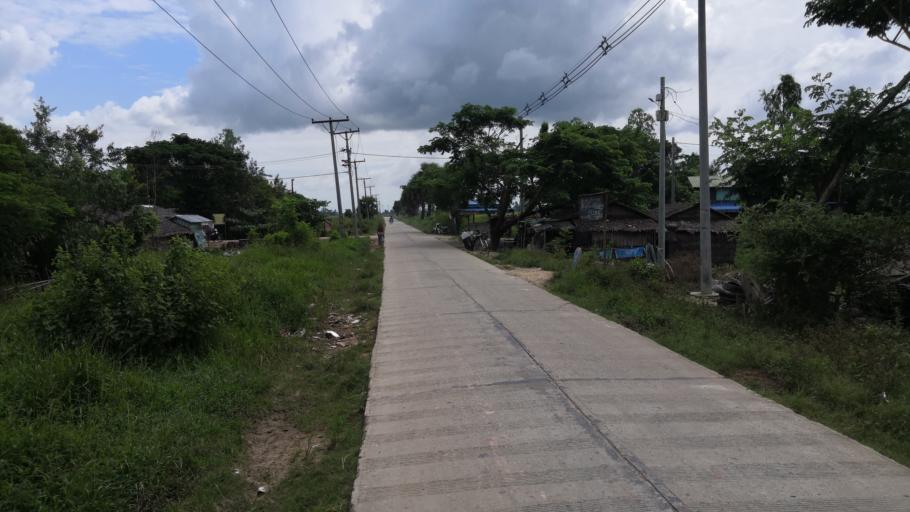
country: MM
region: Yangon
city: Kanbe
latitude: 16.4352
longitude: 96.1601
